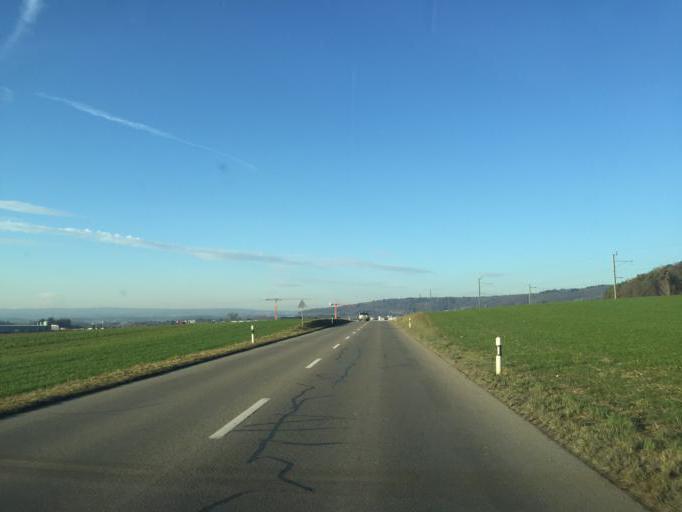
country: CH
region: Thurgau
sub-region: Frauenfeld District
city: Diessenhofen
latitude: 47.6679
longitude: 8.7672
